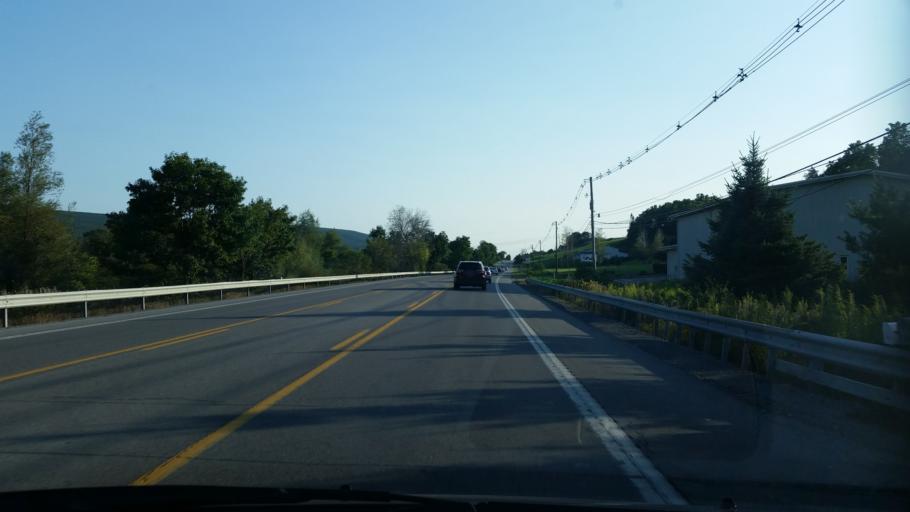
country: US
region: Pennsylvania
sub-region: Blair County
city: Bellwood
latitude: 40.5849
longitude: -78.3260
